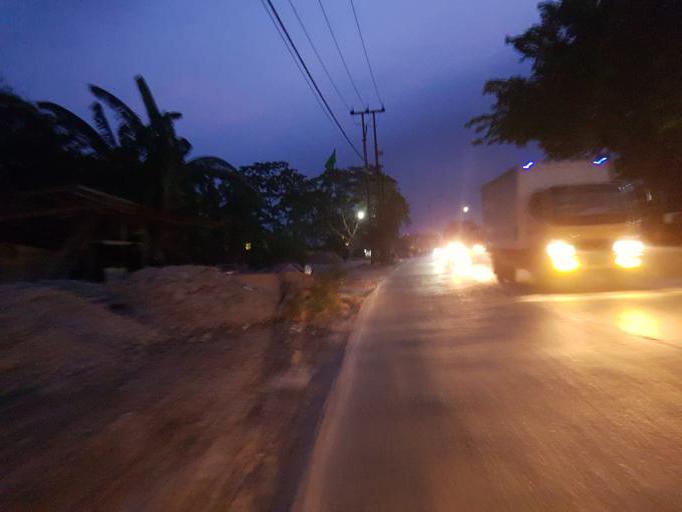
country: ID
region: West Java
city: Serpong
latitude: -6.3145
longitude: 106.6544
